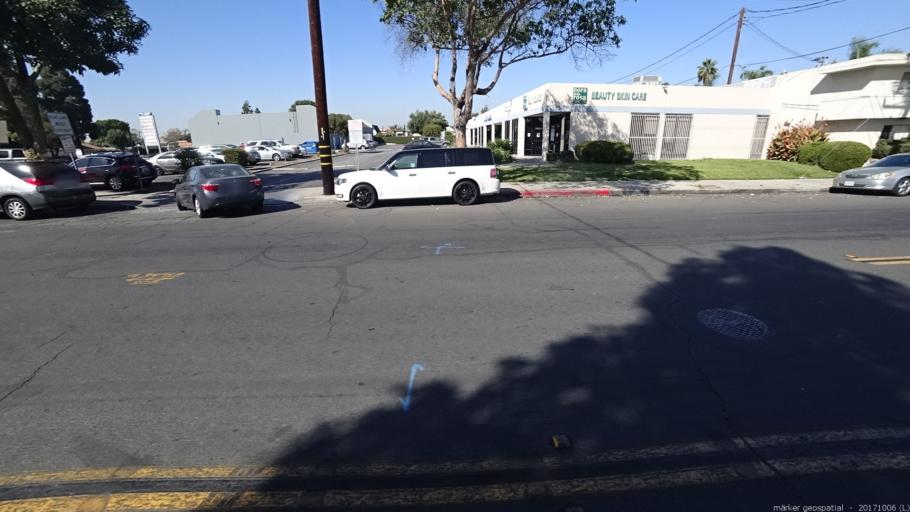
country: US
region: California
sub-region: Orange County
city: Garden Grove
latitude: 33.7813
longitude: -117.9576
